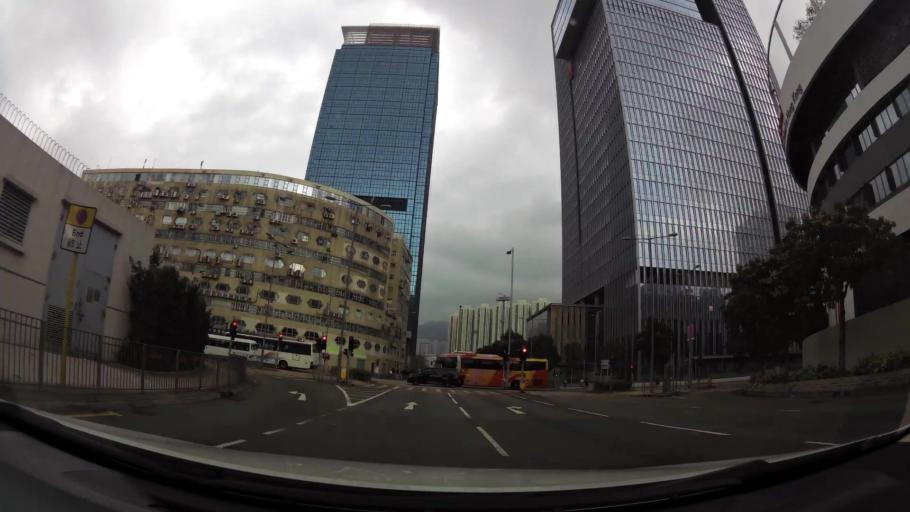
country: HK
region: Kowloon City
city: Kowloon
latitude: 22.3248
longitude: 114.2060
